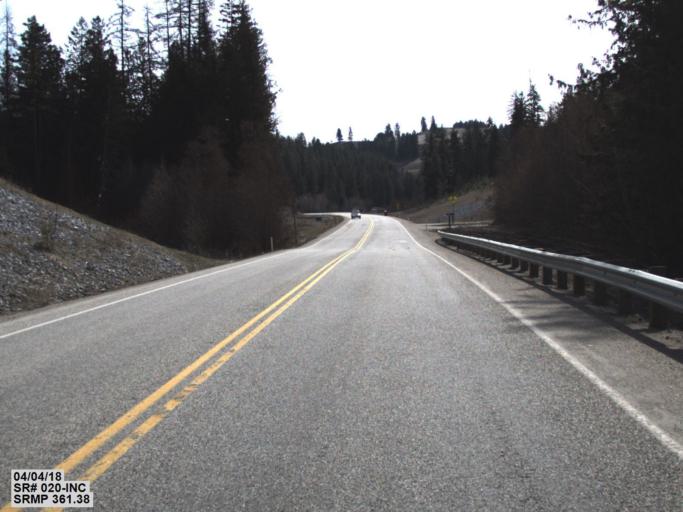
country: US
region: Washington
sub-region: Stevens County
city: Colville
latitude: 48.5144
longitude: -117.7800
